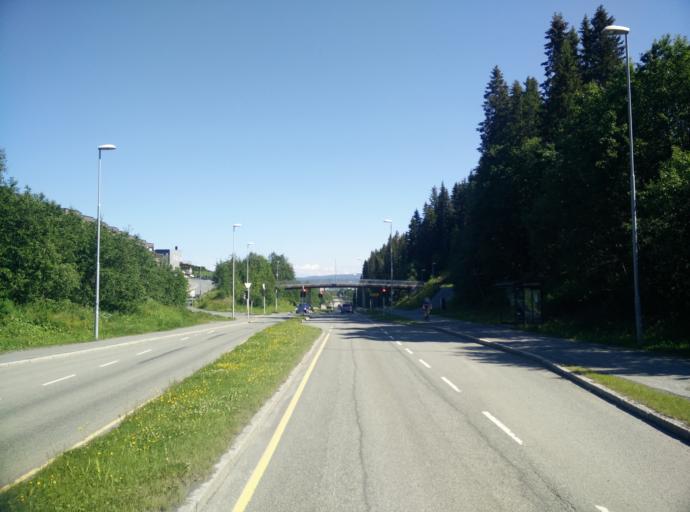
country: NO
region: Sor-Trondelag
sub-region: Trondheim
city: Trondheim
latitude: 63.3759
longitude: 10.3214
